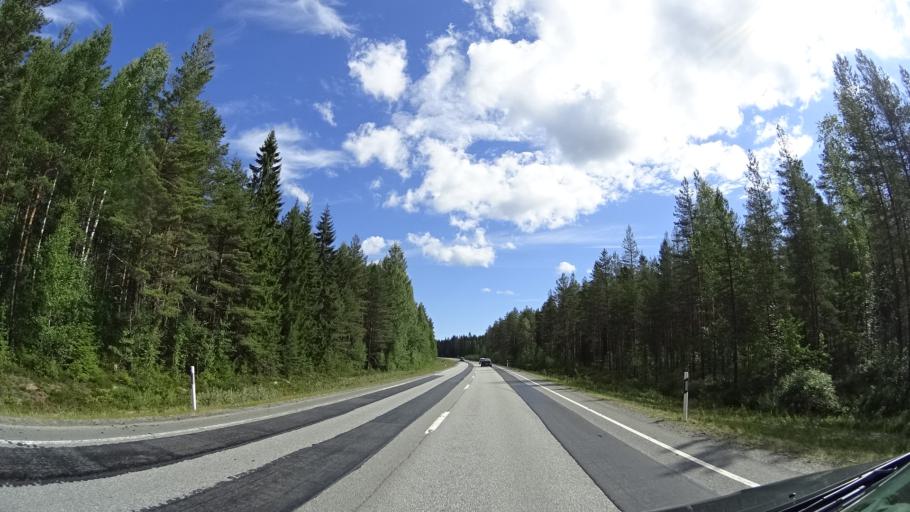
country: FI
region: Pirkanmaa
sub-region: Luoteis-Pirkanmaa
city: Kihnioe
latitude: 62.1312
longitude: 23.1317
